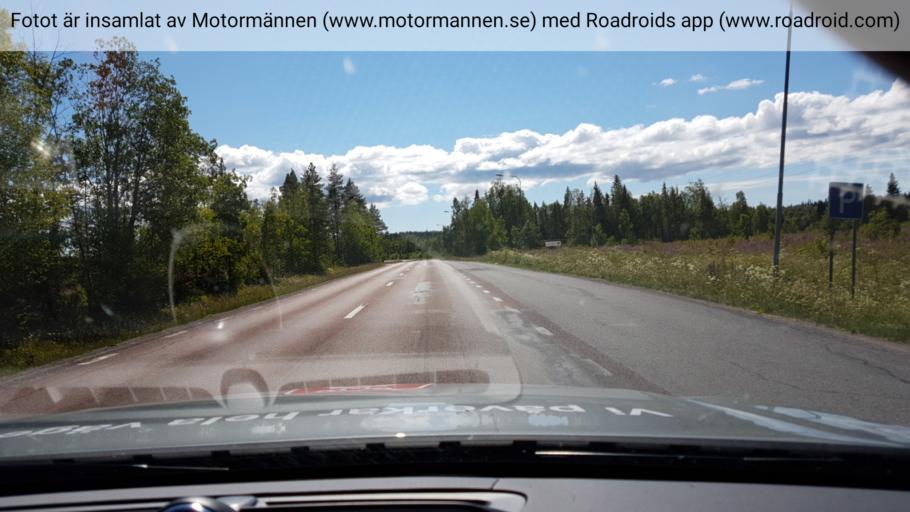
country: SE
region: Jaemtland
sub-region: Stroemsunds Kommun
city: Stroemsund
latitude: 63.8359
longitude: 15.5191
